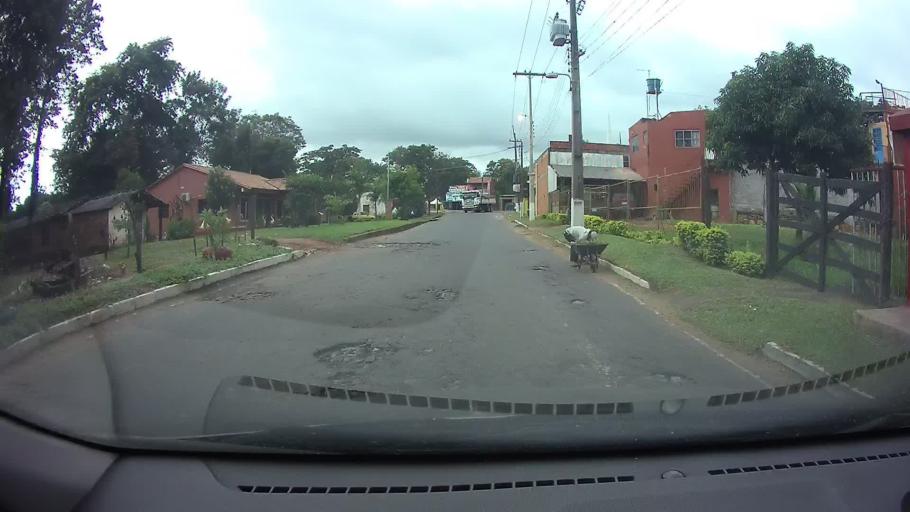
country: PY
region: Central
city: San Antonio
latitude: -25.4329
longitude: -57.5375
